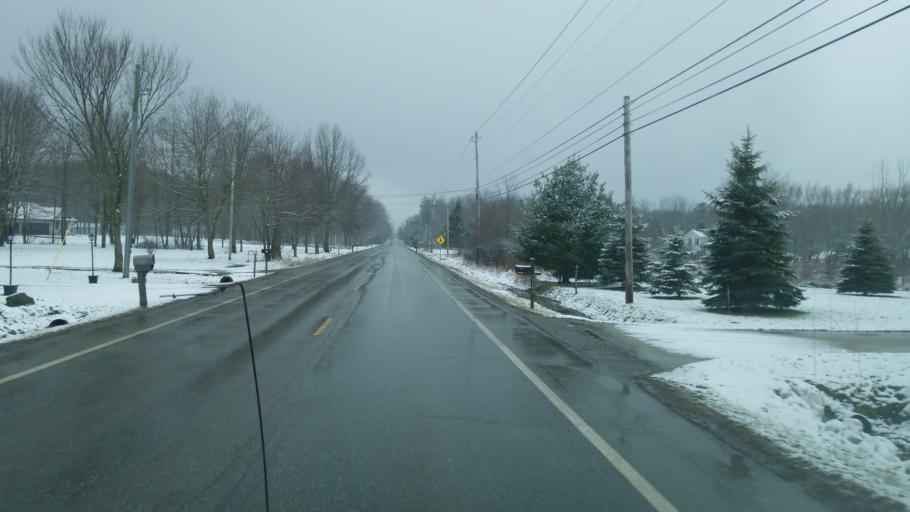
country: US
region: Ohio
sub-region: Portage County
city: Hiram
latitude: 41.3101
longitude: -81.1686
